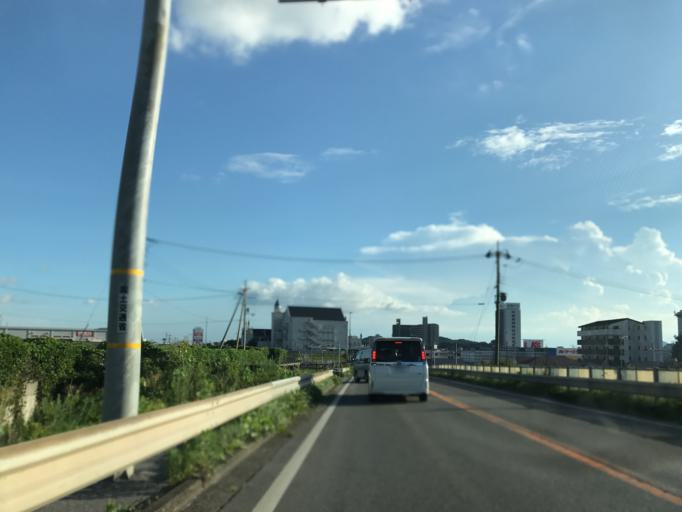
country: JP
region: Shiga Prefecture
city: Hikone
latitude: 35.2733
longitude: 136.2677
